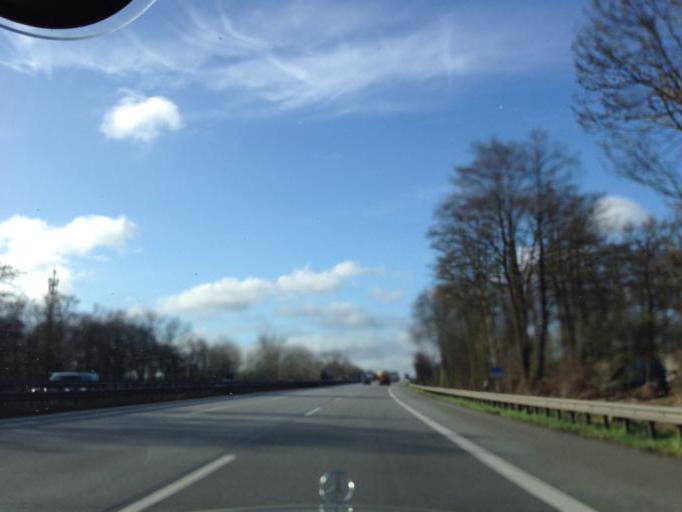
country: DE
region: Hamburg
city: Harburg
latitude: 53.4515
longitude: 10.0284
